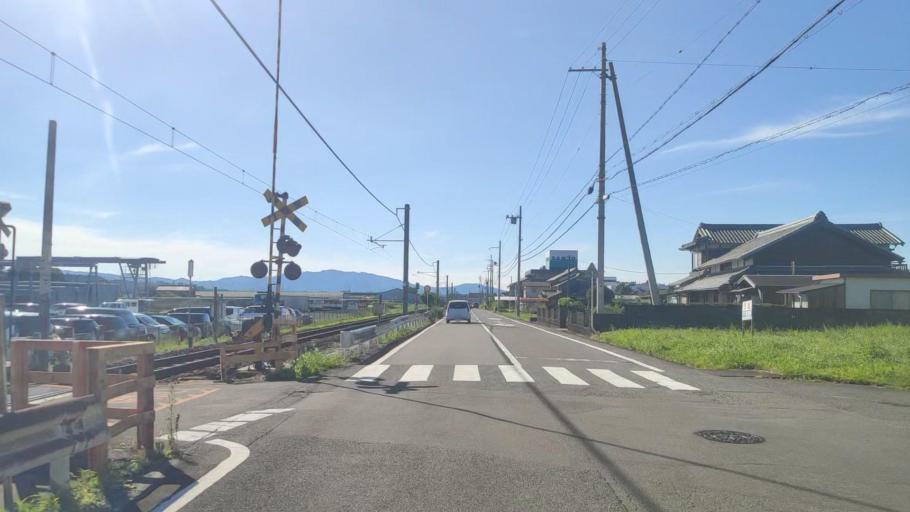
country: JP
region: Shiga Prefecture
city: Minakuchicho-matoba
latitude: 34.8966
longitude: 136.2200
